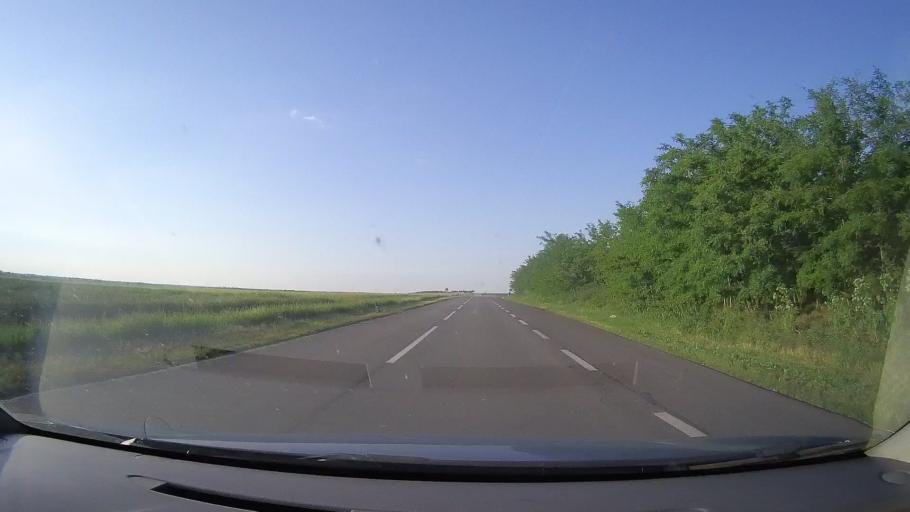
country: RS
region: Autonomna Pokrajina Vojvodina
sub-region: Juznobanatski Okrug
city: Vrsac
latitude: 45.1865
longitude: 21.2973
